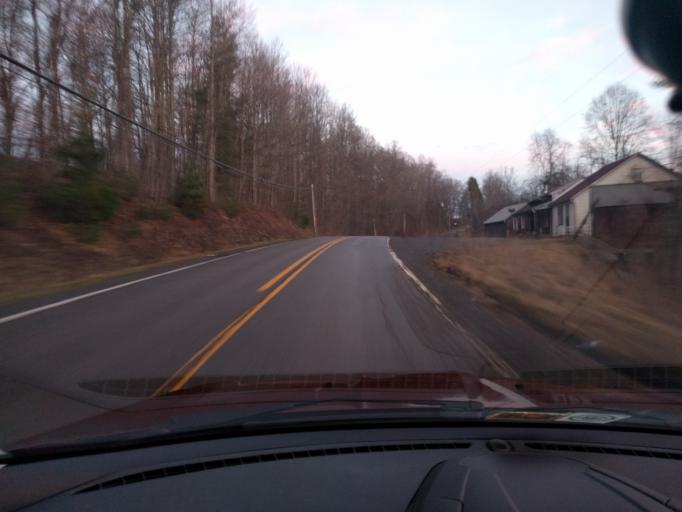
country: US
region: West Virginia
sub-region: Greenbrier County
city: Rainelle
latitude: 38.0012
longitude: -80.8793
